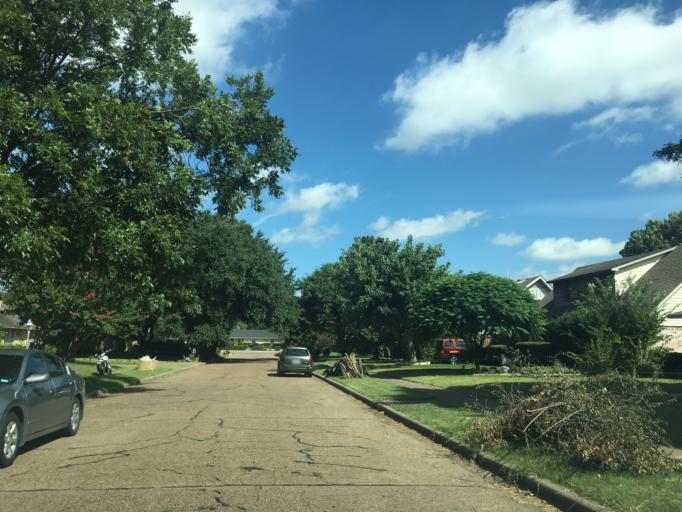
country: US
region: Texas
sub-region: Dallas County
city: Garland
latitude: 32.8450
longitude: -96.6596
